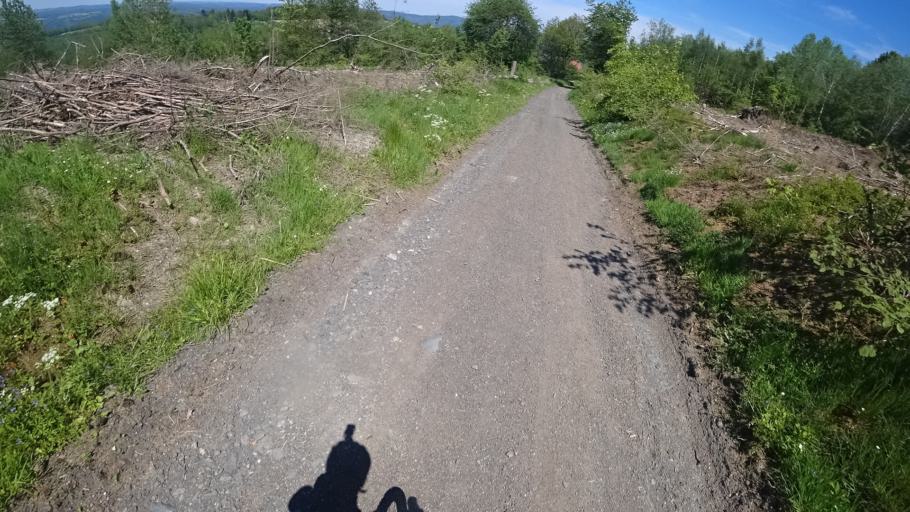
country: DE
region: Rheinland-Pfalz
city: Steineroth
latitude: 50.7572
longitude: 7.8505
